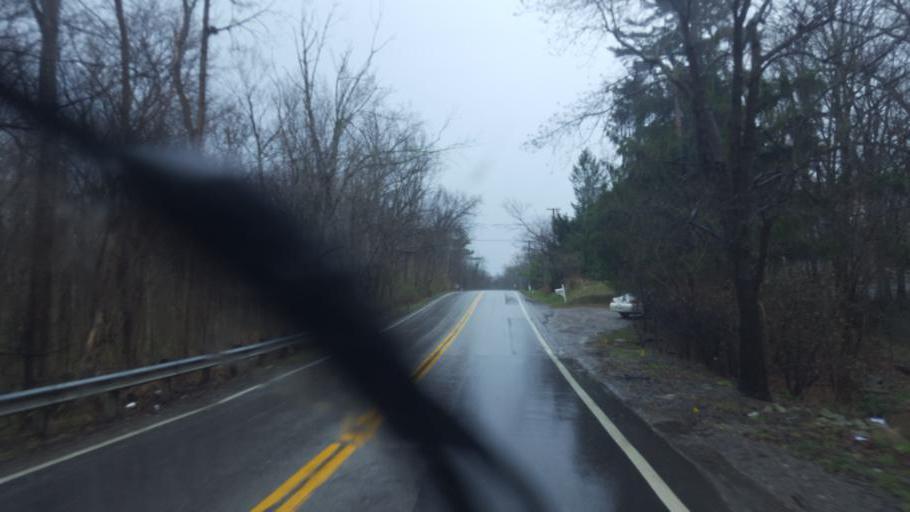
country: US
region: Ohio
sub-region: Delaware County
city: Powell
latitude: 40.1355
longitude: -83.0368
